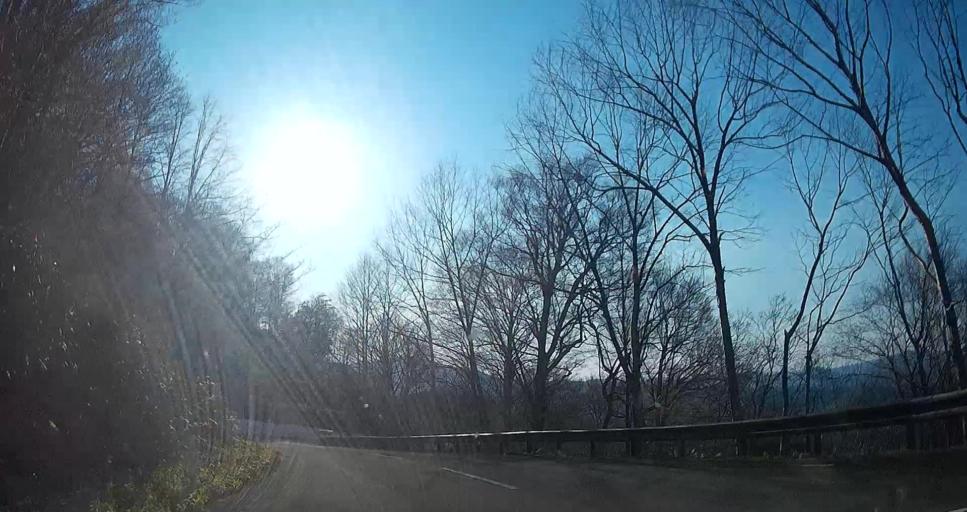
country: JP
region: Aomori
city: Mutsu
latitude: 41.3091
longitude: 141.1200
